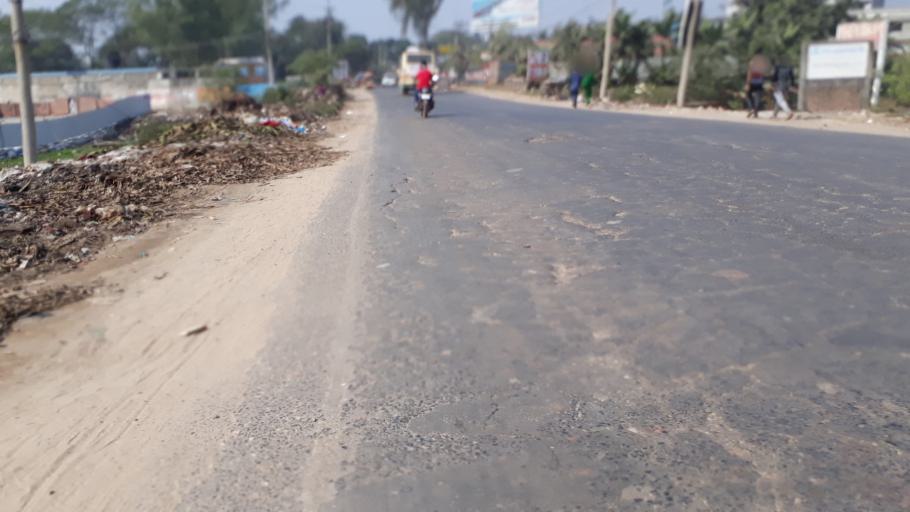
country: BD
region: Dhaka
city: Tungi
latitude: 23.9061
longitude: 90.3224
